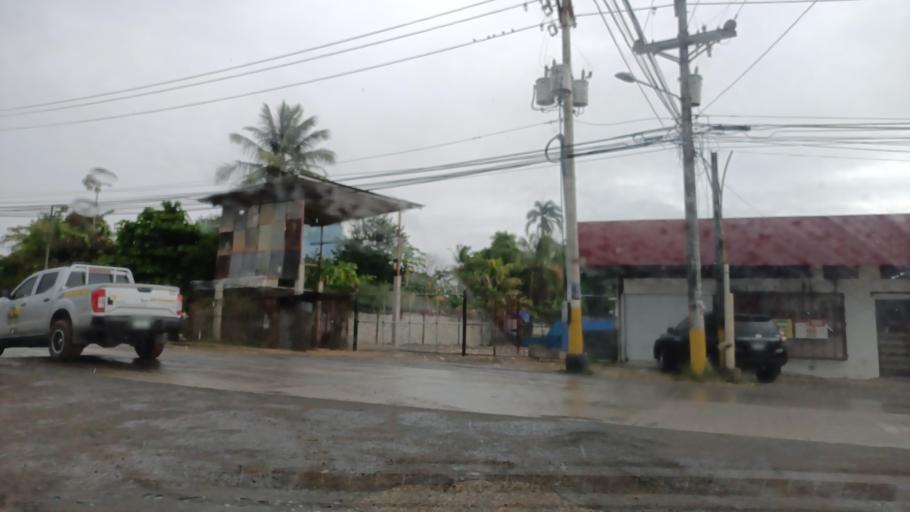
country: PA
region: Panama
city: Caimitillo
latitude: 9.1638
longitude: -79.5490
